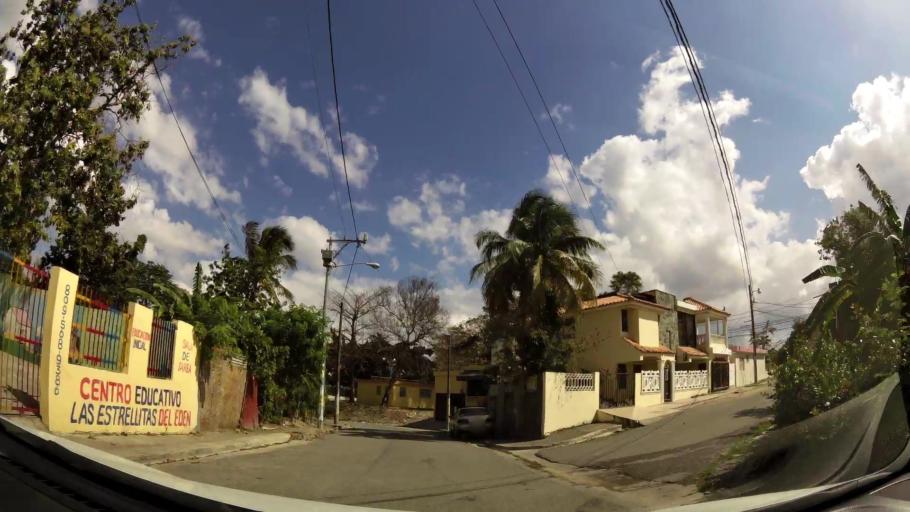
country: DO
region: Nacional
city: Ensanche Luperon
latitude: 18.5397
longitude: -69.9015
